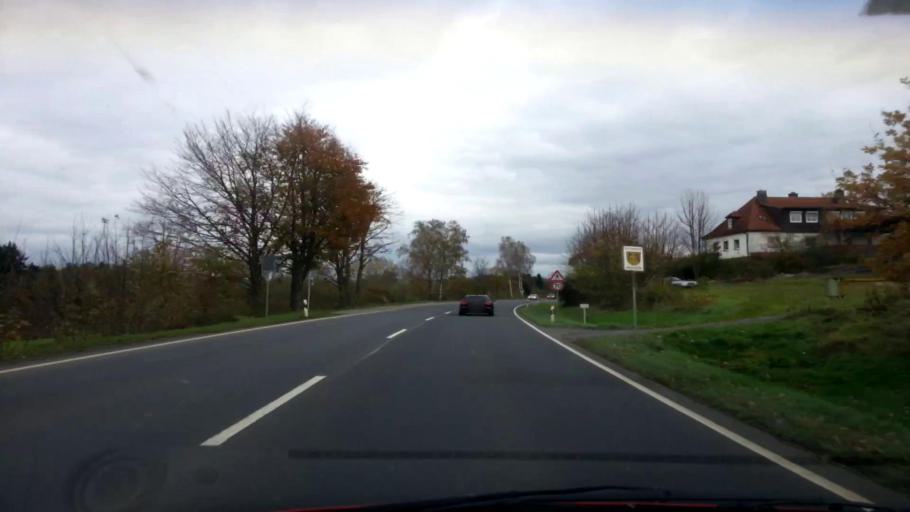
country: DE
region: Bavaria
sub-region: Upper Franconia
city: Kueps Oberfranken
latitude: 50.1831
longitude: 11.2496
